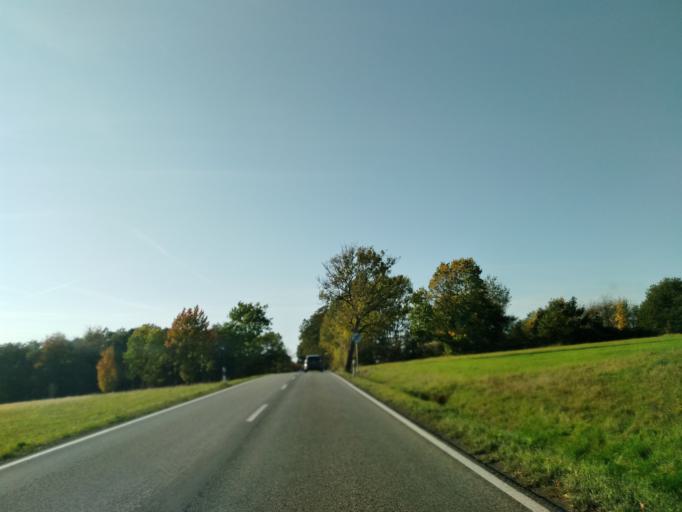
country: DE
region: Rheinland-Pfalz
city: Asbach
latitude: 50.6707
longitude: 7.3731
